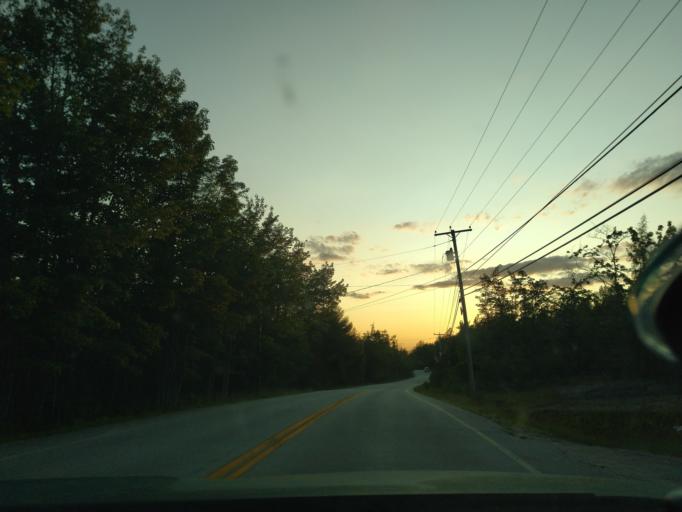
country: US
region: Maine
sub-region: Hancock County
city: Gouldsboro
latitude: 44.3923
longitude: -68.0554
